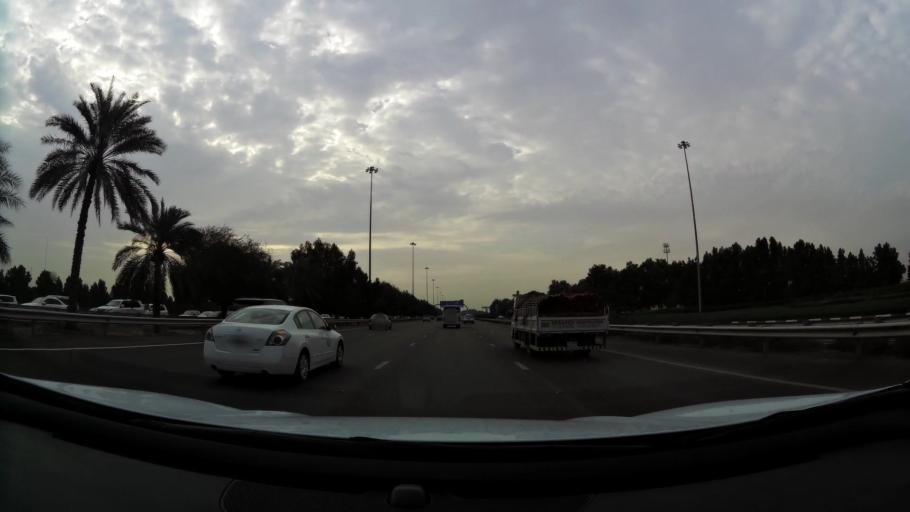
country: AE
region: Abu Dhabi
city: Abu Dhabi
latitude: 24.3260
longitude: 54.5867
